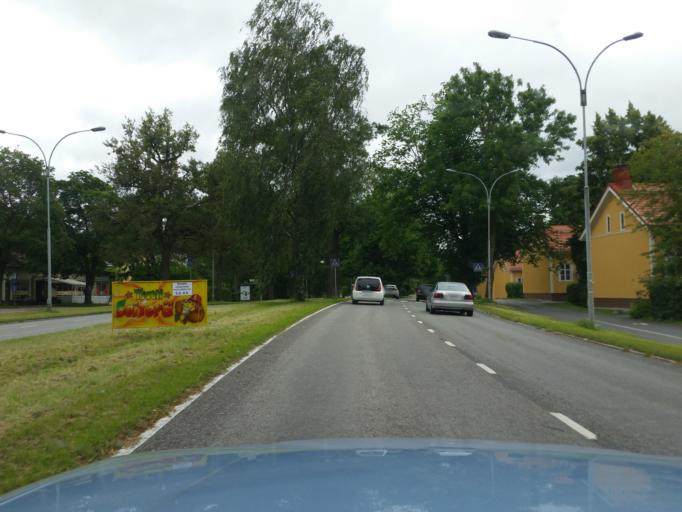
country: FI
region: Varsinais-Suomi
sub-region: Turku
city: Turku
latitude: 60.4393
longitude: 22.2910
